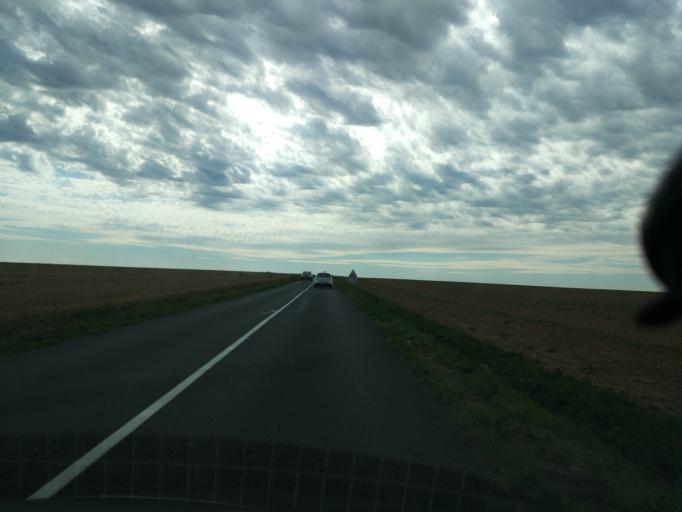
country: FR
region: Ile-de-France
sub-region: Departement de l'Essonne
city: Gometz-la-Ville
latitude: 48.6627
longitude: 2.1265
